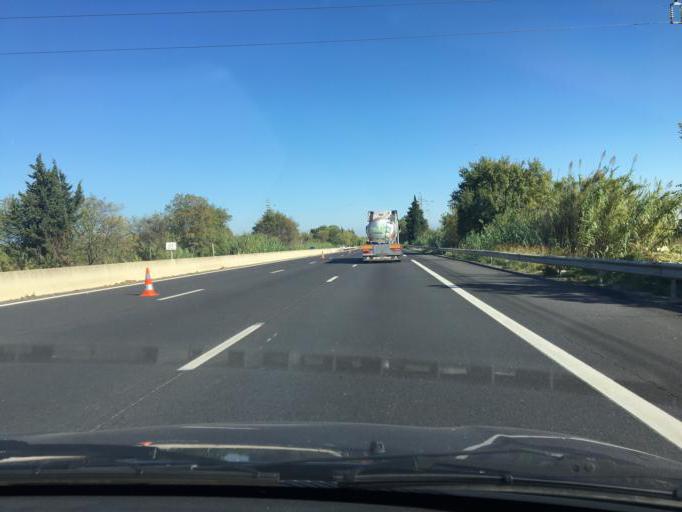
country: FR
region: Languedoc-Roussillon
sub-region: Departement du Gard
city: Caissargues
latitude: 43.8246
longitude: 4.3855
